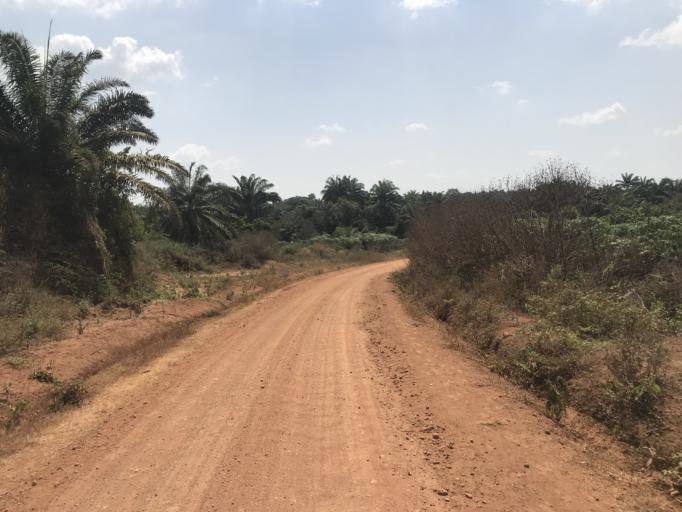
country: NG
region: Osun
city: Ifon
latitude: 7.9558
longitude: 4.4949
